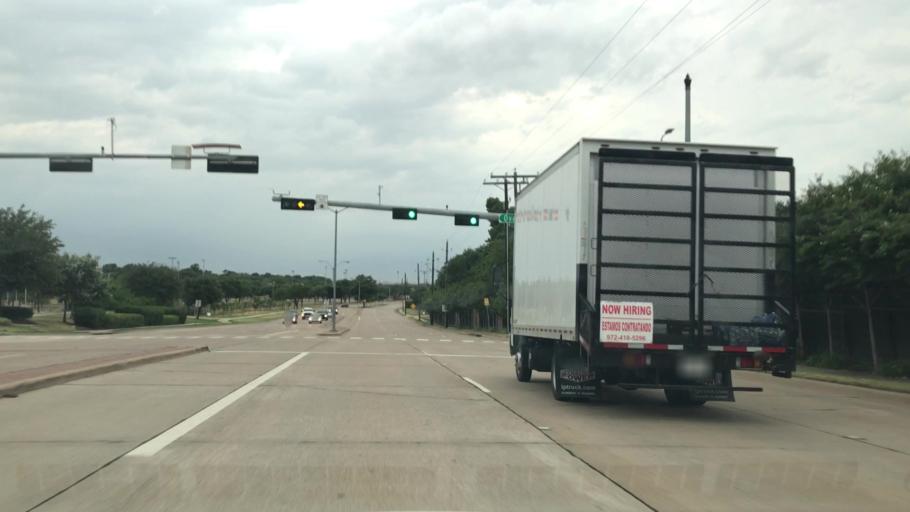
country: US
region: Texas
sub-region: Dallas County
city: Carrollton
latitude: 32.9717
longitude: -96.8940
